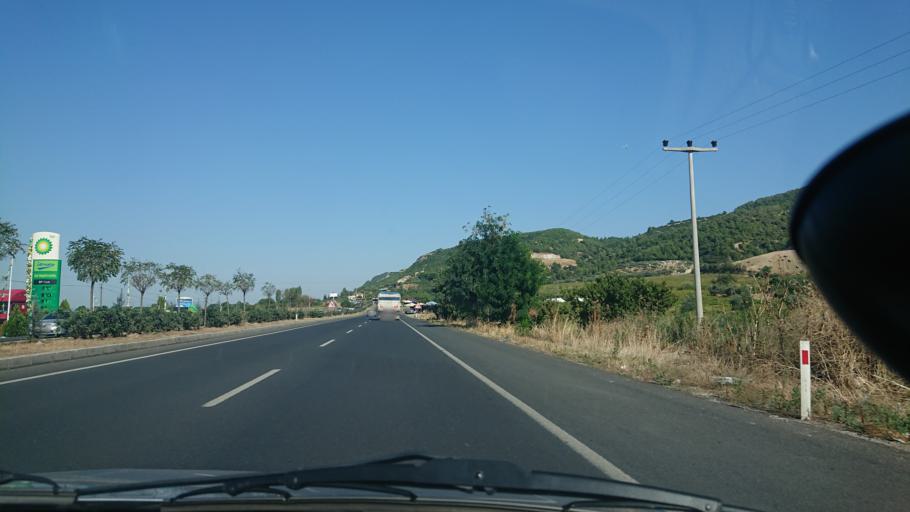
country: TR
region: Manisa
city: Ahmetli
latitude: 38.4839
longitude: 27.8225
